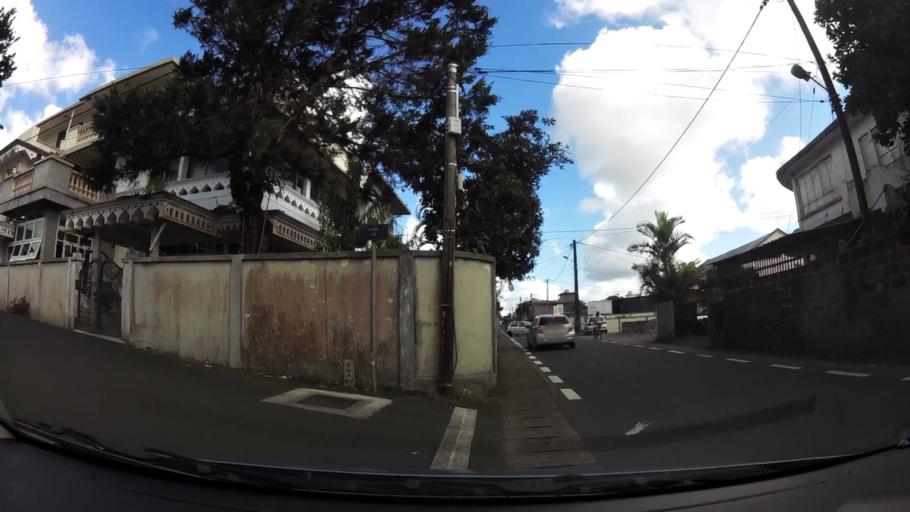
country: MU
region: Plaines Wilhems
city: Curepipe
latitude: -20.3289
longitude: 57.5281
